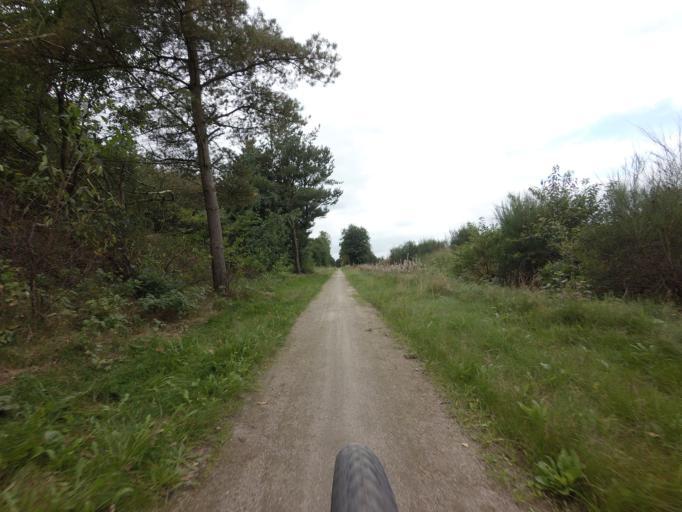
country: DK
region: South Denmark
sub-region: Billund Kommune
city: Grindsted
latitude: 55.7991
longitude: 8.9994
